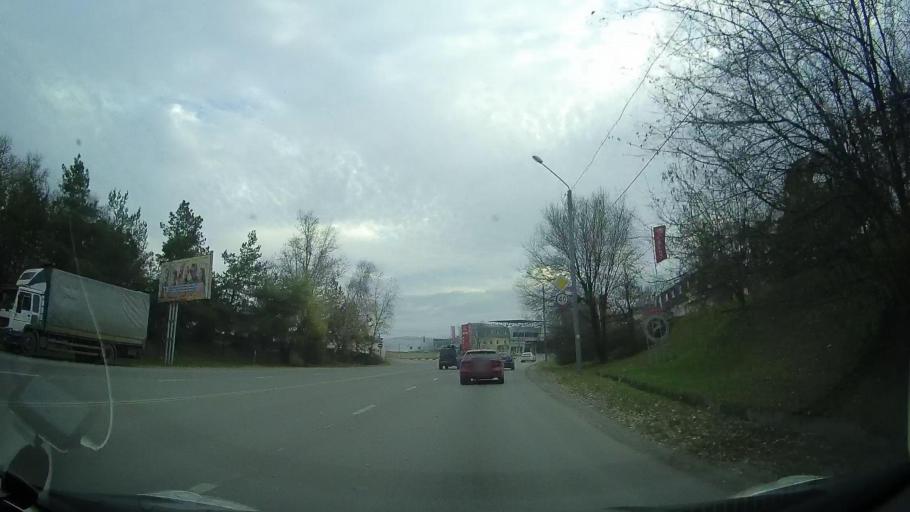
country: RU
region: Rostov
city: Aksay
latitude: 47.2452
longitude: 39.8420
